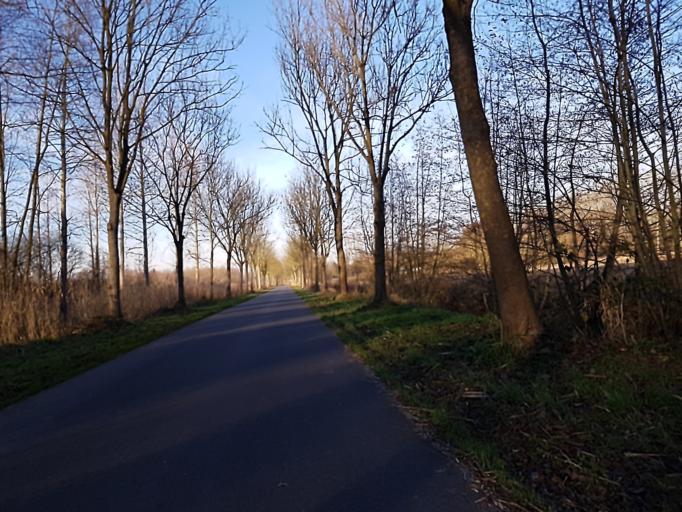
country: BE
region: Flanders
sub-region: Provincie Antwerpen
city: Puurs
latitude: 51.1089
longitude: 4.2866
